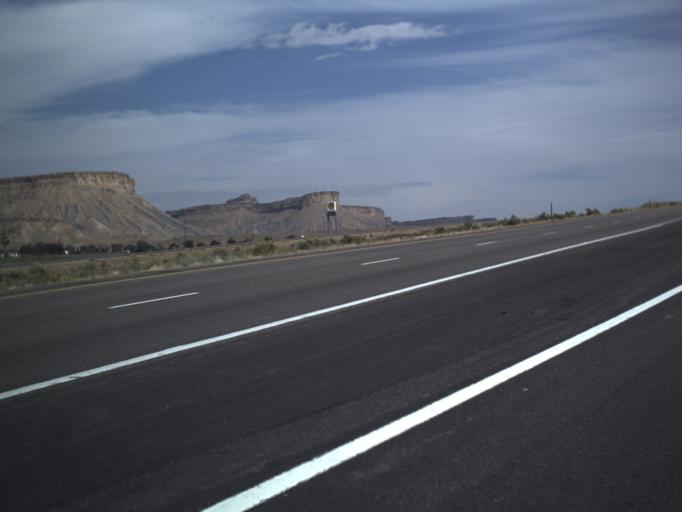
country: US
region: Utah
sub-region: Grand County
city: Moab
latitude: 38.9601
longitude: -109.7287
